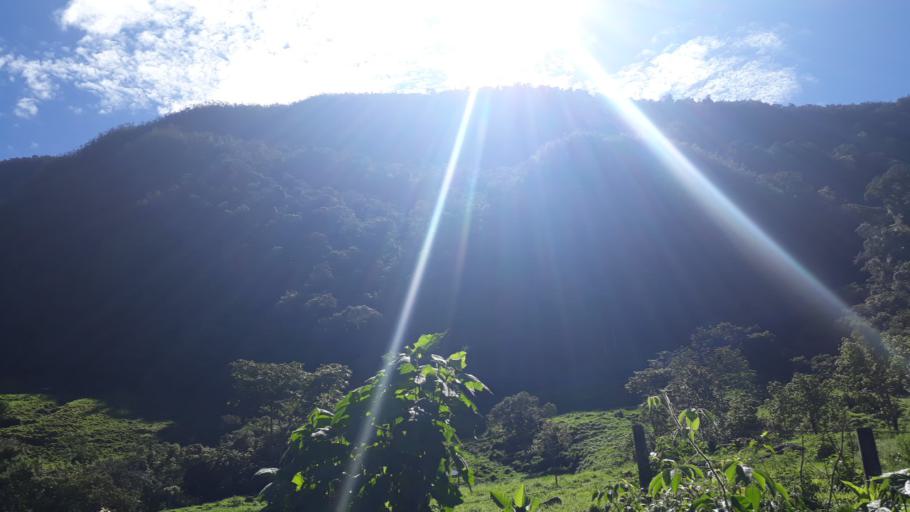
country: CO
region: Casanare
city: Nunchia
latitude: 5.6668
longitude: -72.4227
